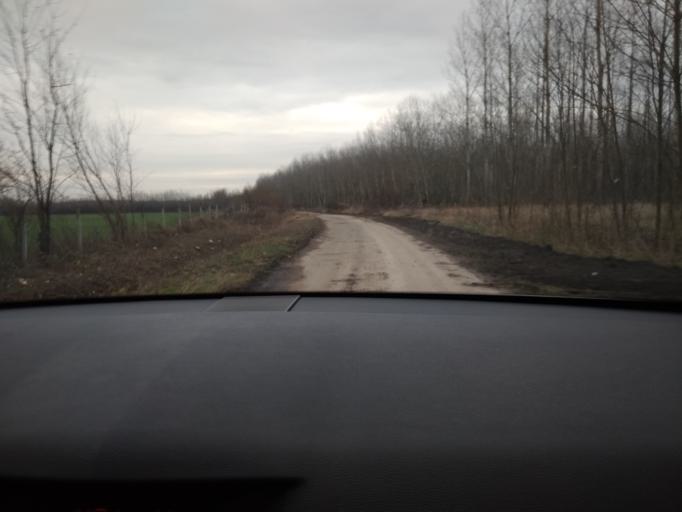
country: HU
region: Szabolcs-Szatmar-Bereg
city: Apagy
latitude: 47.9924
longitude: 21.8920
